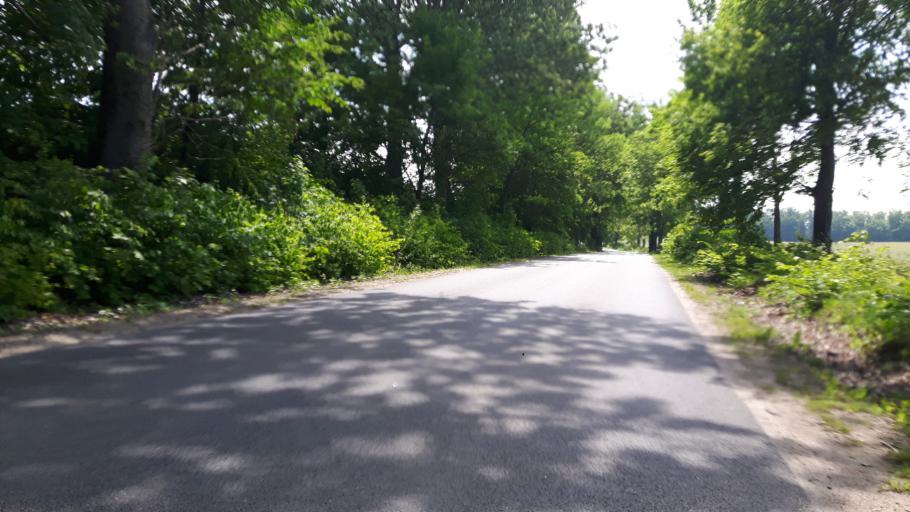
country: PL
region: Pomeranian Voivodeship
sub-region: Powiat wejherowski
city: Choczewo
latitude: 54.7536
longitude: 17.7922
